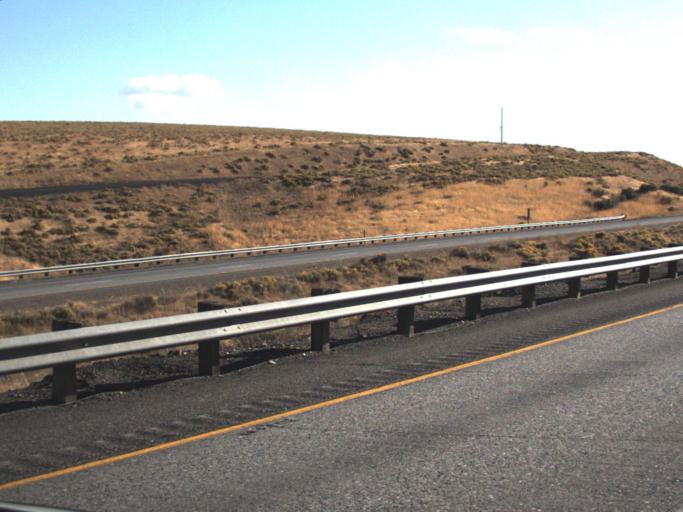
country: US
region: Washington
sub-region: Benton County
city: Highland
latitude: 46.0925
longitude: -119.2230
